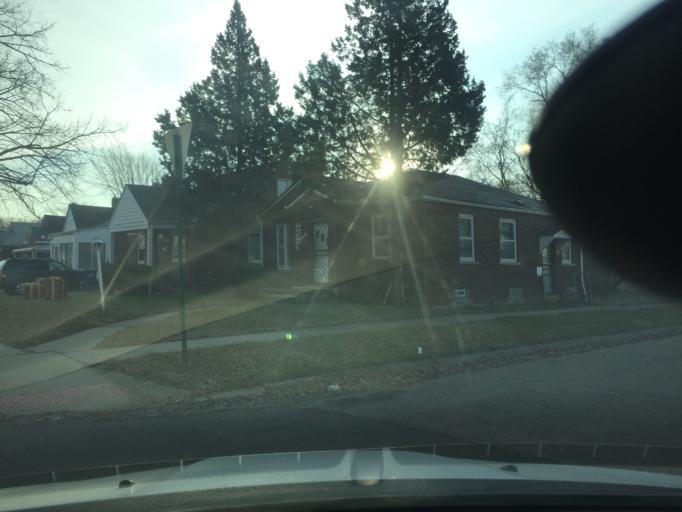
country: US
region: Michigan
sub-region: Wayne County
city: Harper Woods
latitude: 42.4330
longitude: -82.9581
